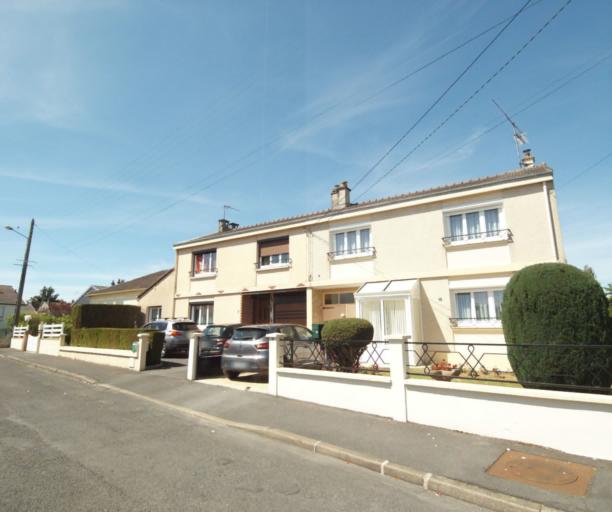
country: FR
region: Champagne-Ardenne
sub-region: Departement des Ardennes
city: La Francheville
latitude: 49.7471
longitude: 4.7150
